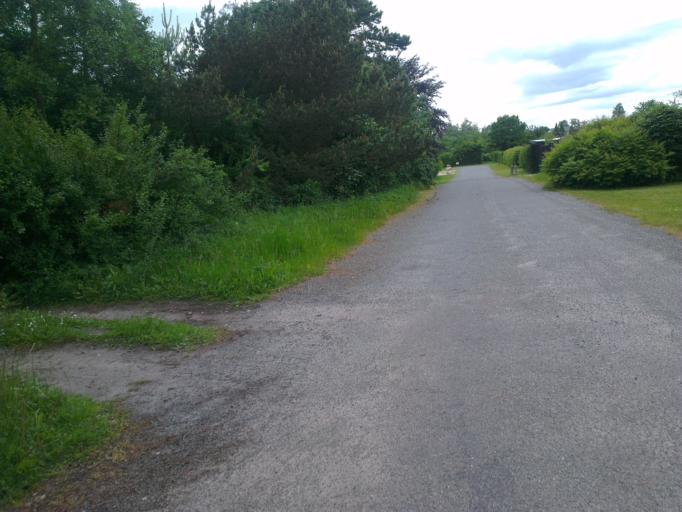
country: DK
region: Capital Region
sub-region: Frederikssund Kommune
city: Frederikssund
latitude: 55.8113
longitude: 12.0404
